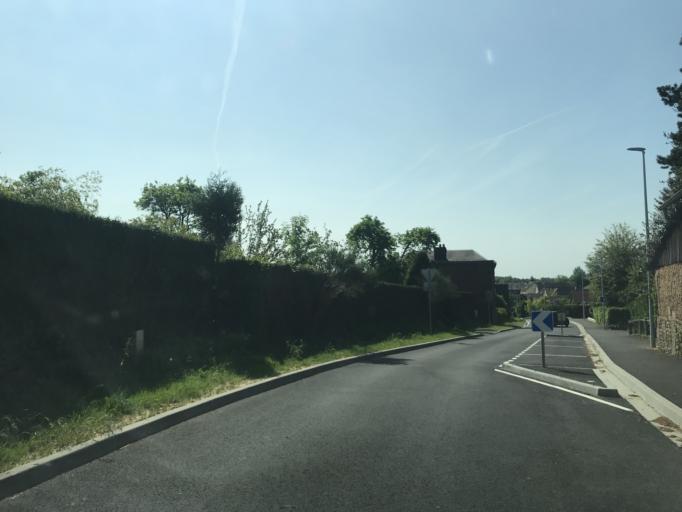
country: FR
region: Haute-Normandie
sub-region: Departement de la Seine-Maritime
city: Ymare
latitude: 49.3655
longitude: 1.1592
